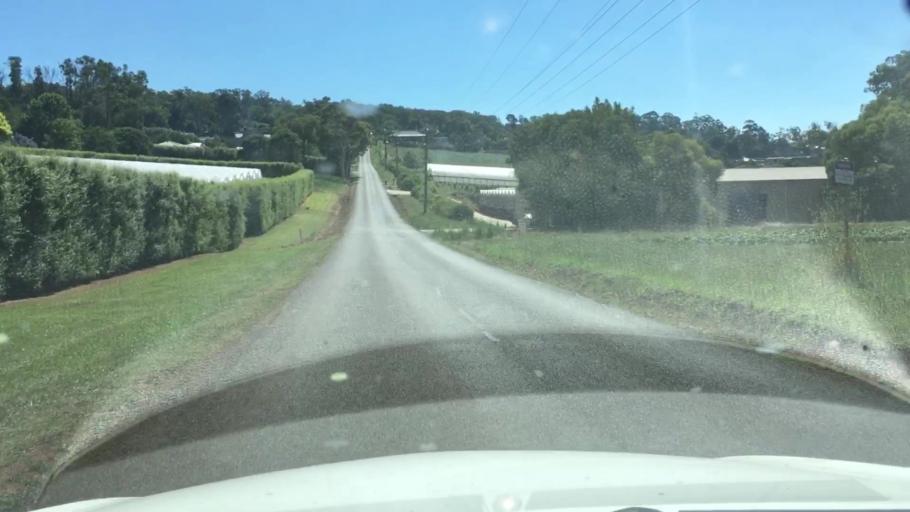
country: AU
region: Victoria
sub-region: Yarra Ranges
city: Mount Evelyn
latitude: -37.8193
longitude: 145.4202
